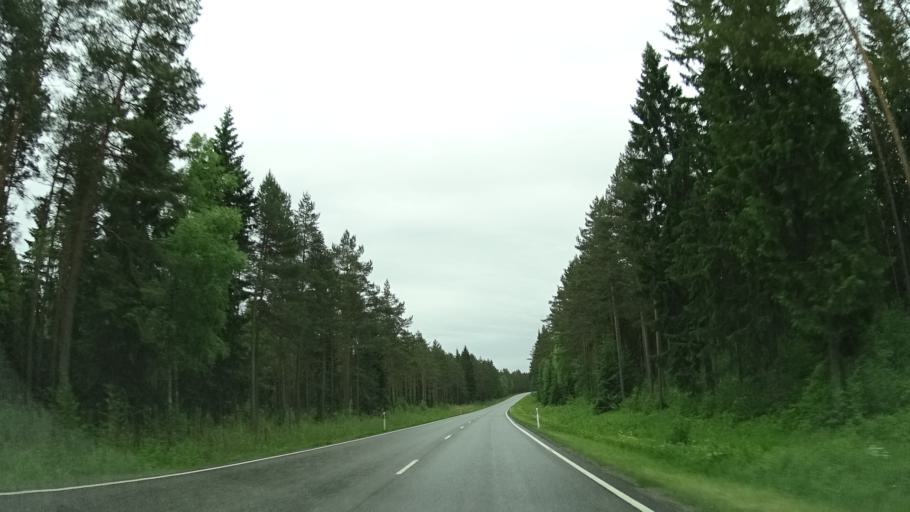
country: FI
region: Varsinais-Suomi
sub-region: Salo
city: Pernioe
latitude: 60.1142
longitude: 23.2118
